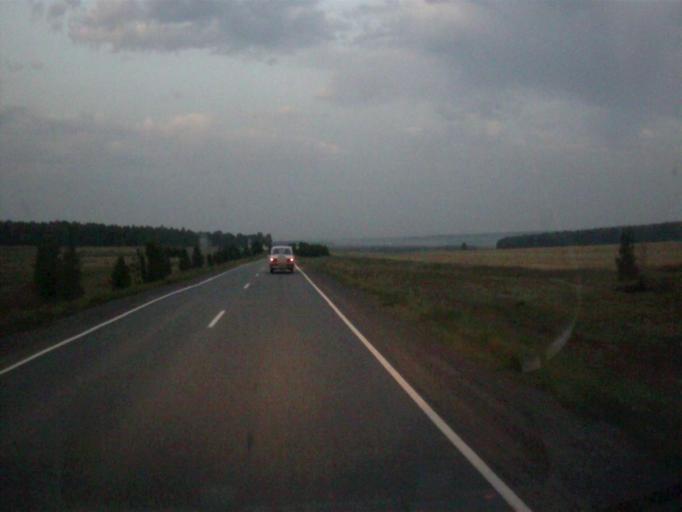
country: RU
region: Chelyabinsk
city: Argayash
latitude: 55.2088
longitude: 60.8343
